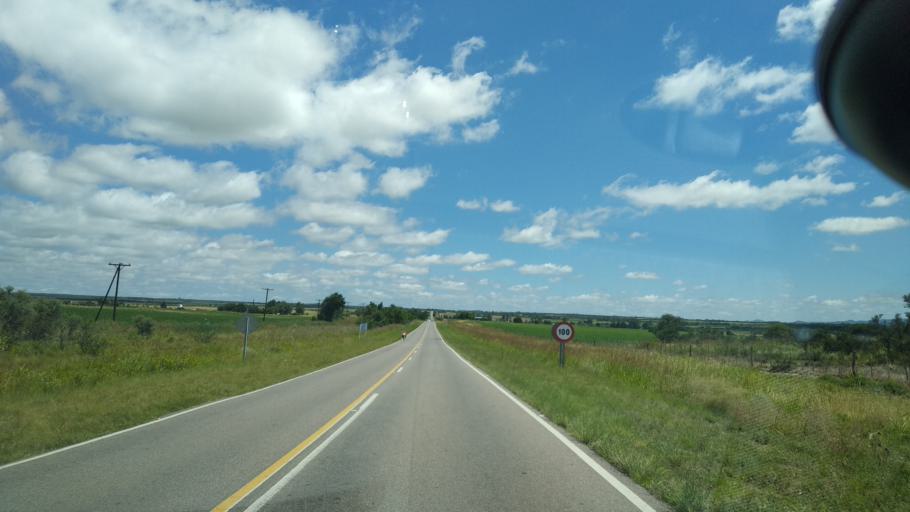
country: AR
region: Cordoba
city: Villa Cura Brochero
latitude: -31.6514
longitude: -65.0994
